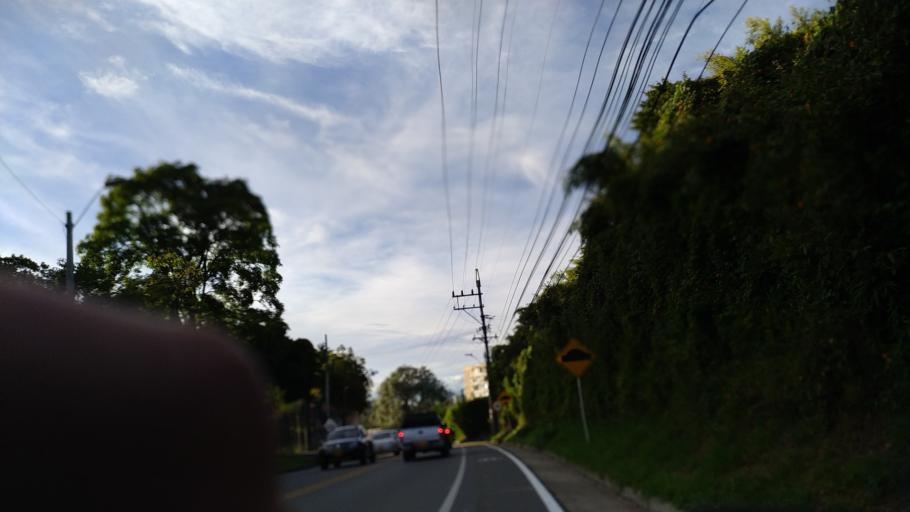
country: CO
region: Antioquia
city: Rionegro
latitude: 6.1375
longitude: -75.3782
